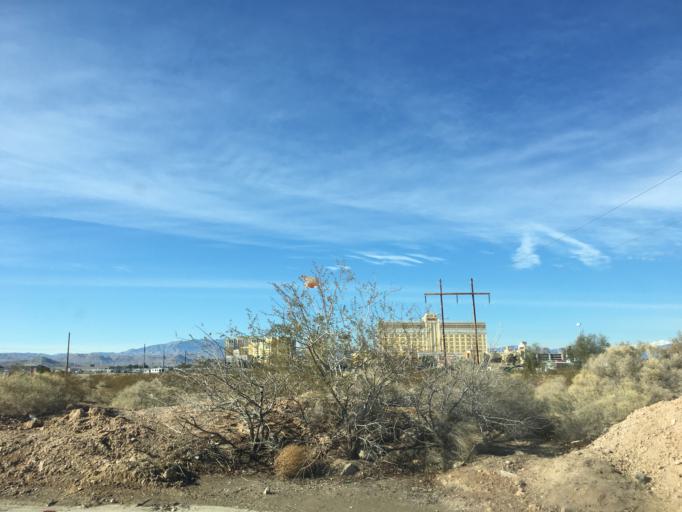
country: US
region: Nevada
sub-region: Clark County
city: Enterprise
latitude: 36.0099
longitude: -115.1657
